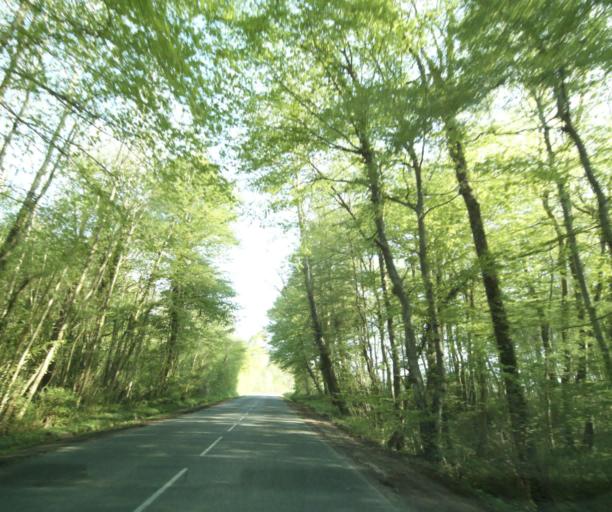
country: FR
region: Ile-de-France
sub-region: Departement de Seine-et-Marne
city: Vernou-la-Celle-sur-Seine
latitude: 48.4047
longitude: 2.8345
